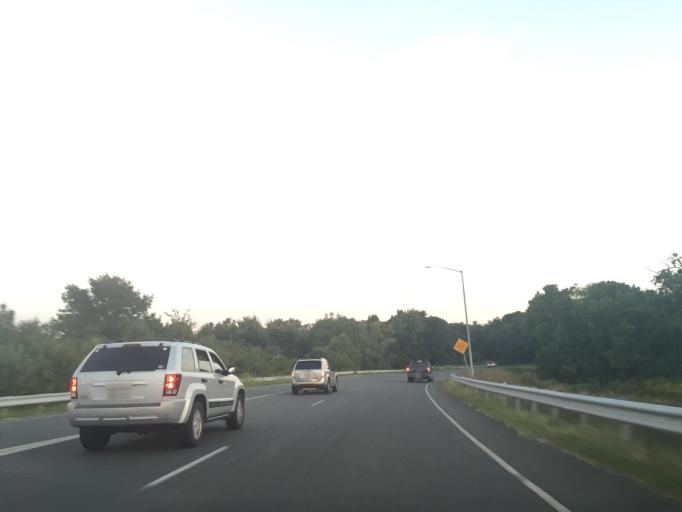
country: US
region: Maryland
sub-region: Harford County
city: Bel Air North
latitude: 39.5567
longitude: -76.3696
